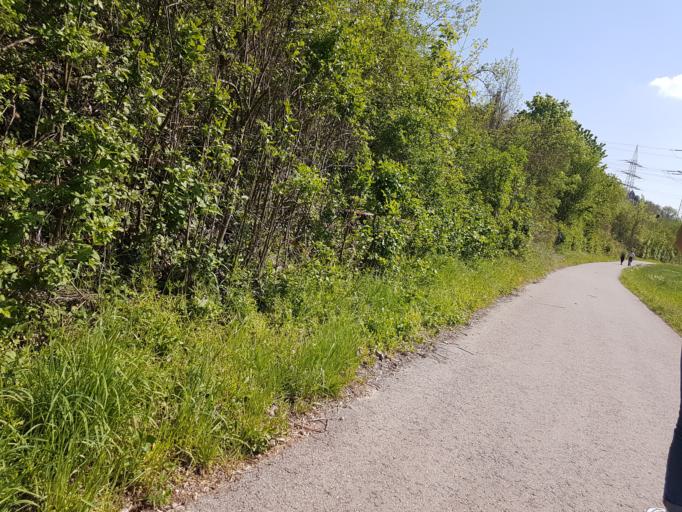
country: DE
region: Baden-Wuerttemberg
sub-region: Regierungsbezirk Stuttgart
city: Besigheim
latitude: 48.9869
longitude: 9.1513
